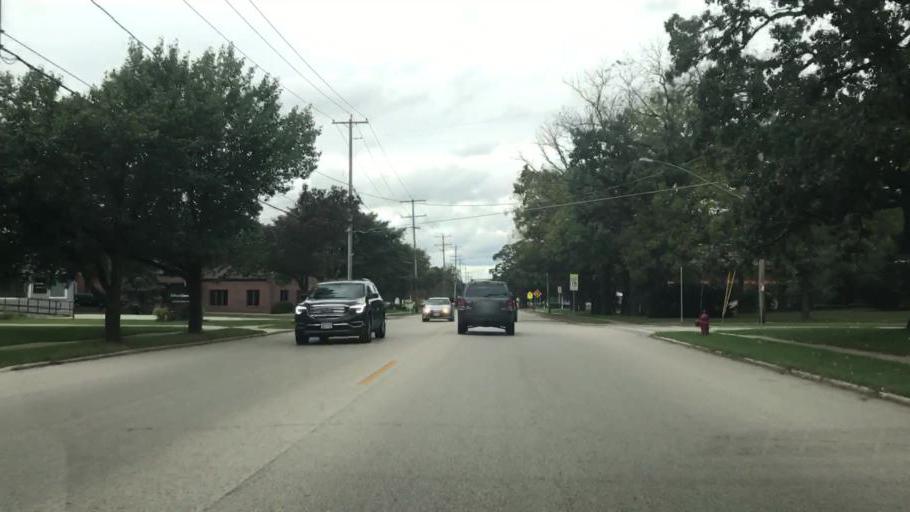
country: US
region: Wisconsin
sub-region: Waukesha County
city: Mukwonago
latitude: 42.8690
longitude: -88.3354
